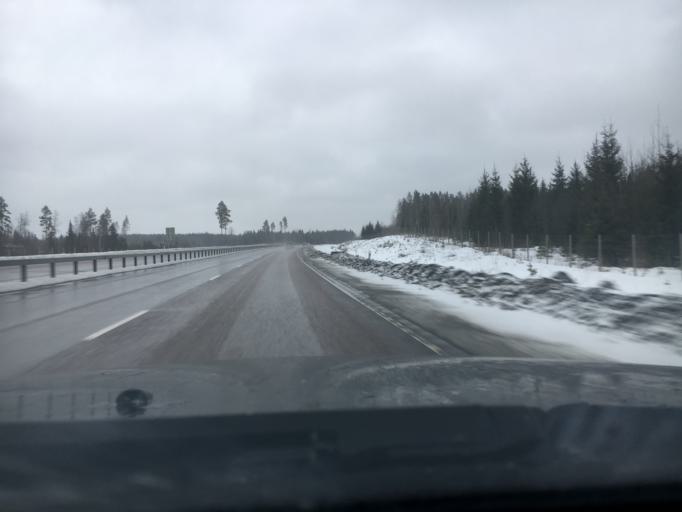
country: FI
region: Central Finland
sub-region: Joutsa
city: Joutsa
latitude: 61.8094
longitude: 26.0924
